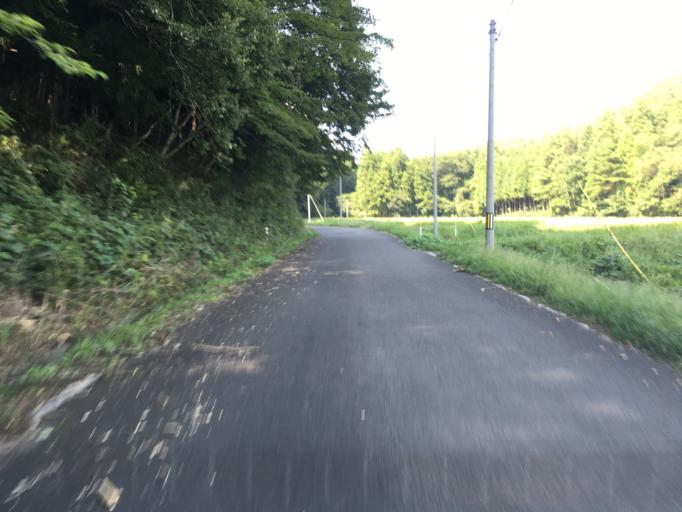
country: JP
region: Fukushima
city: Nihommatsu
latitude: 37.6027
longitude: 140.3833
